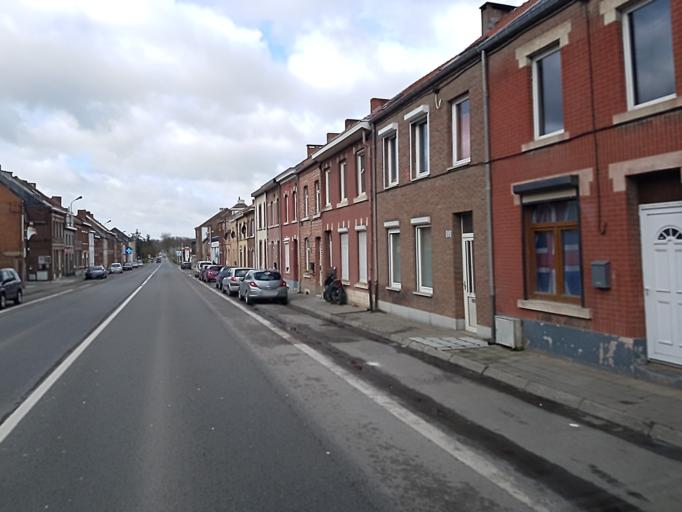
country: BE
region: Wallonia
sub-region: Province du Brabant Wallon
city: Jodoigne
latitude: 50.7182
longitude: 4.8680
